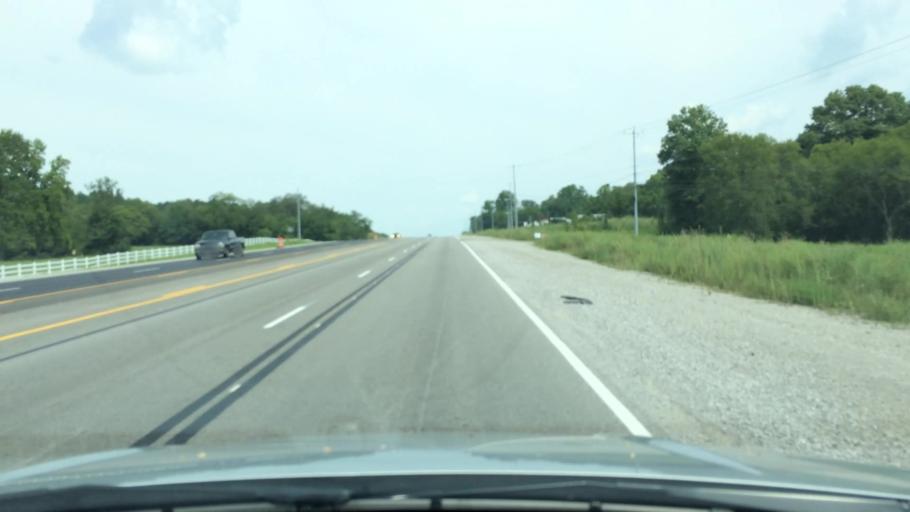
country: US
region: Tennessee
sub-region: Giles County
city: Pulaski
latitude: 35.1590
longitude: -87.0082
